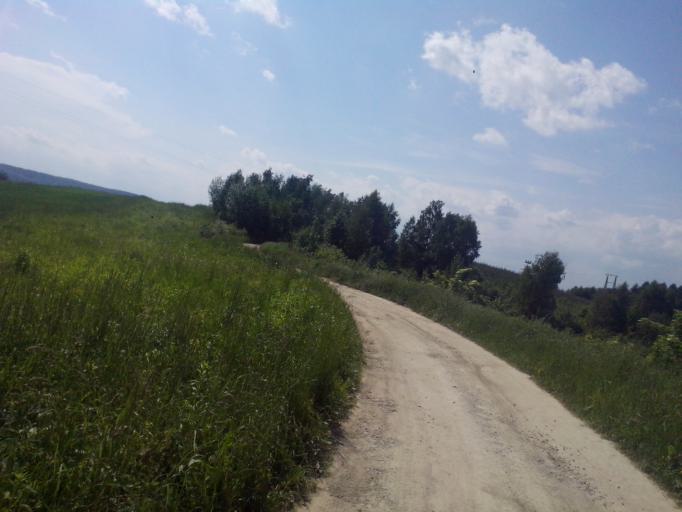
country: PL
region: Subcarpathian Voivodeship
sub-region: Powiat strzyzowski
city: Strzyzow
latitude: 49.8478
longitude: 21.8377
